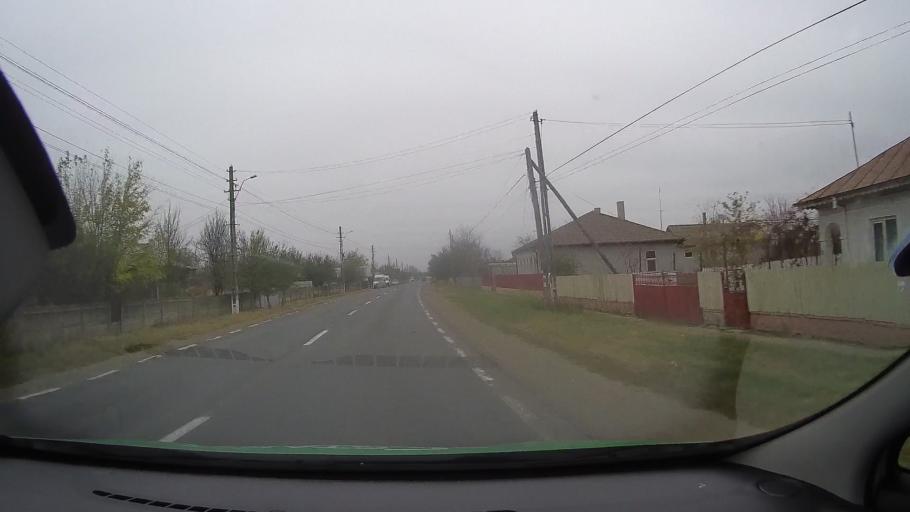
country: RO
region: Braila
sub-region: Comuna Baraganul
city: Baraganul
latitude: 44.8086
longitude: 27.5137
